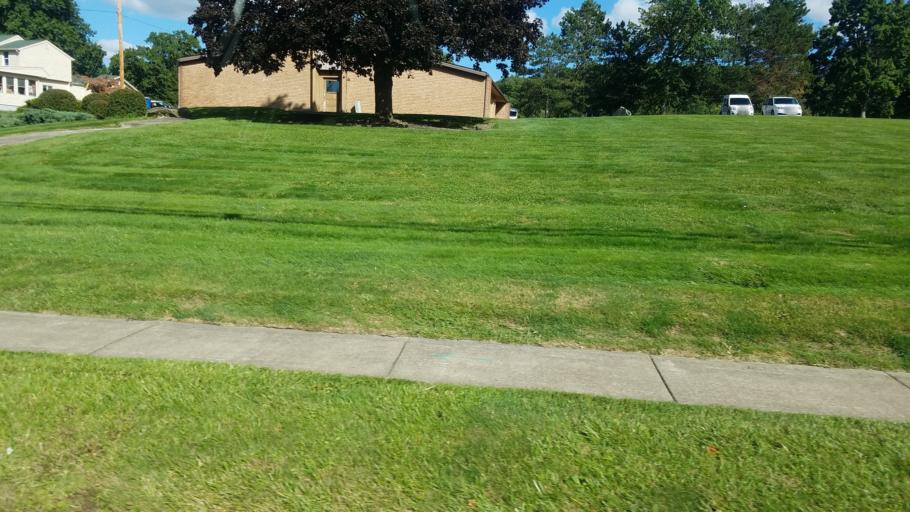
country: US
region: Ohio
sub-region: Trumbull County
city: Mineral Ridge
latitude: 41.1507
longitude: -80.7688
